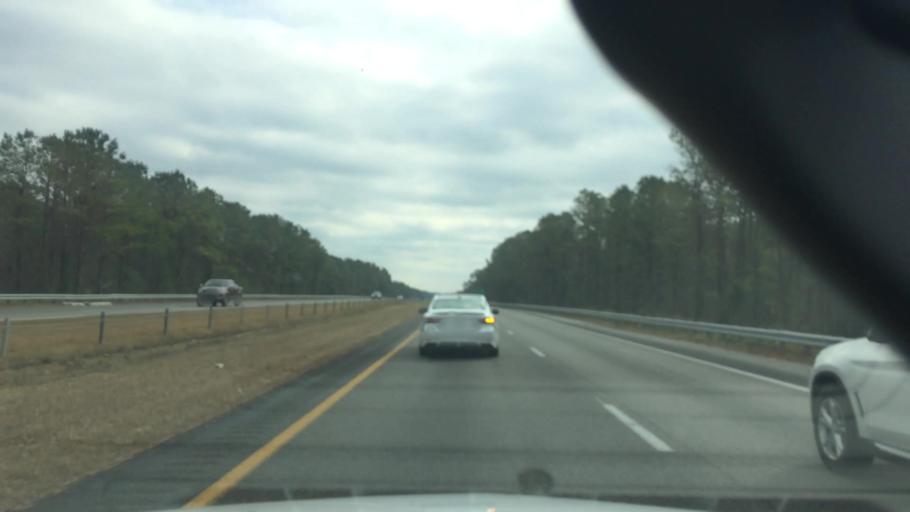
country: US
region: North Carolina
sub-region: New Hanover County
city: Castle Hayne
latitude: 34.3574
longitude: -77.8874
